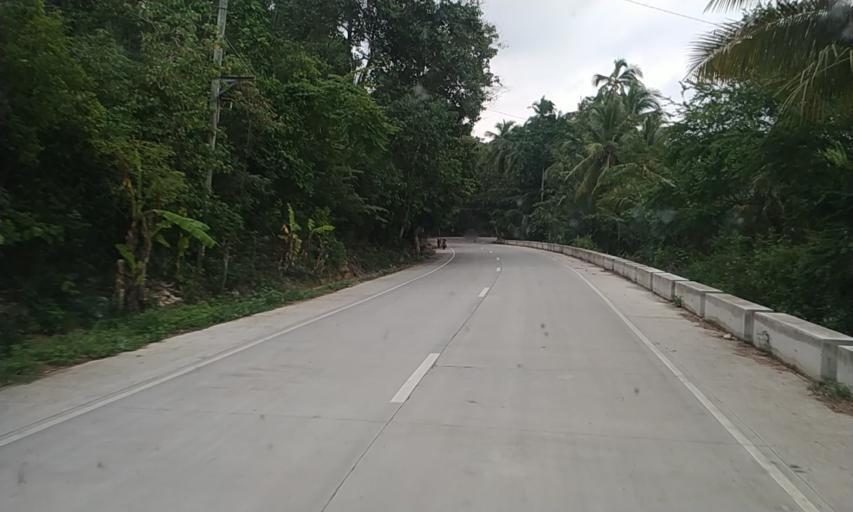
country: PH
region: Central Visayas
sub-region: Province of Negros Oriental
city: Basak
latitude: 10.2027
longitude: 123.2995
